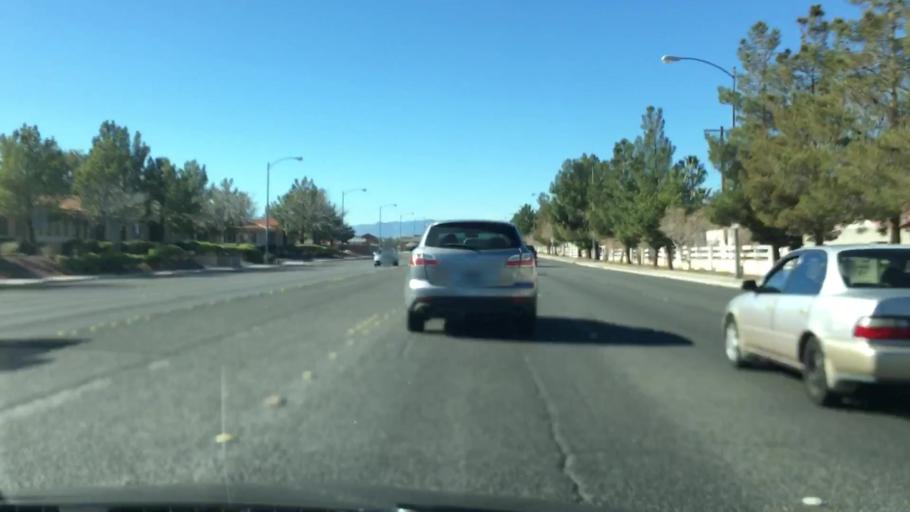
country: US
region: Nevada
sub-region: Clark County
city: Whitney
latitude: 36.0570
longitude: -115.1080
